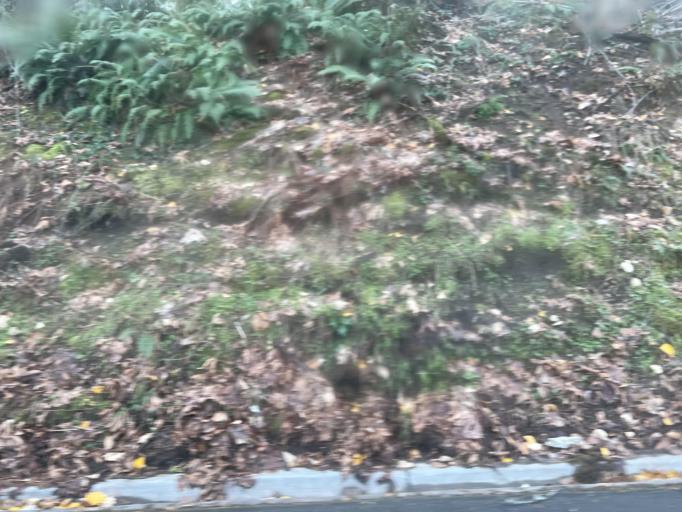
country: US
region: Washington
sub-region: Clark County
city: Washougal
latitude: 45.5385
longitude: -122.2232
